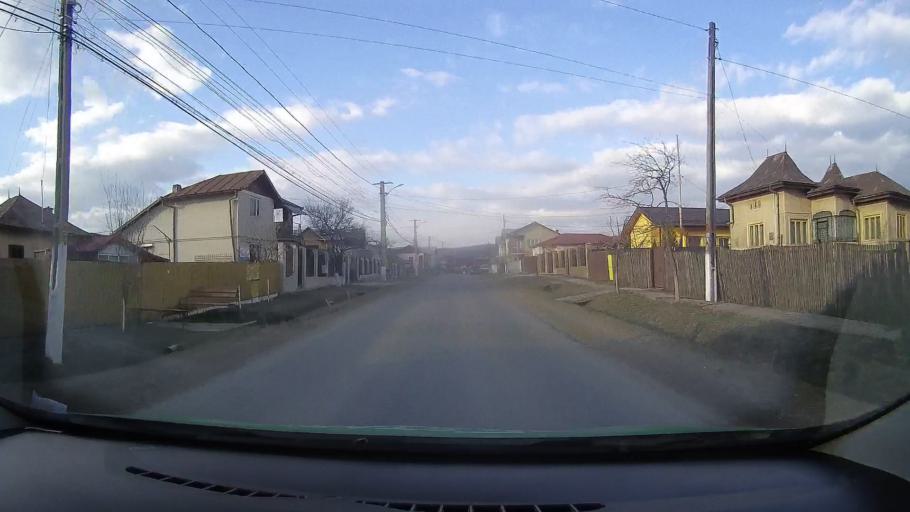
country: RO
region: Dambovita
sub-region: Comuna Ocnita
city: Ocnita
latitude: 44.9853
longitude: 25.5542
